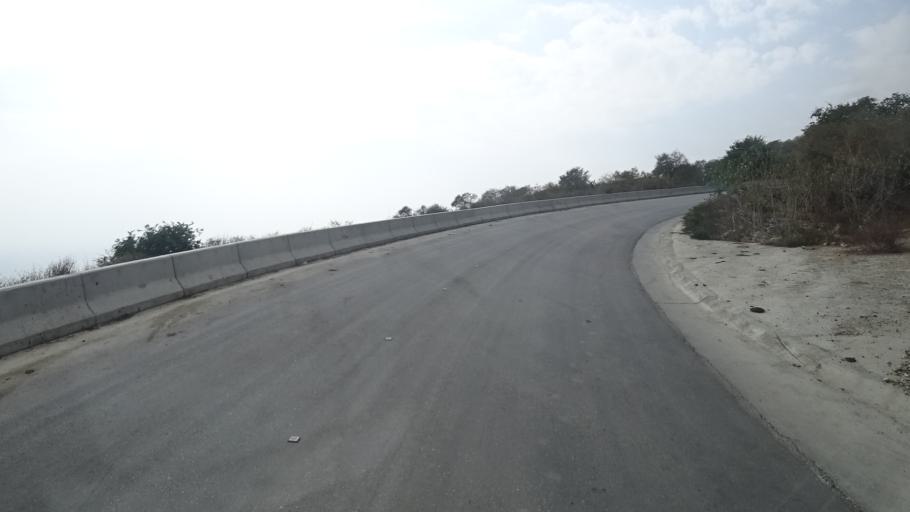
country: YE
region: Al Mahrah
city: Hawf
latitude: 16.7110
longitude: 53.2529
